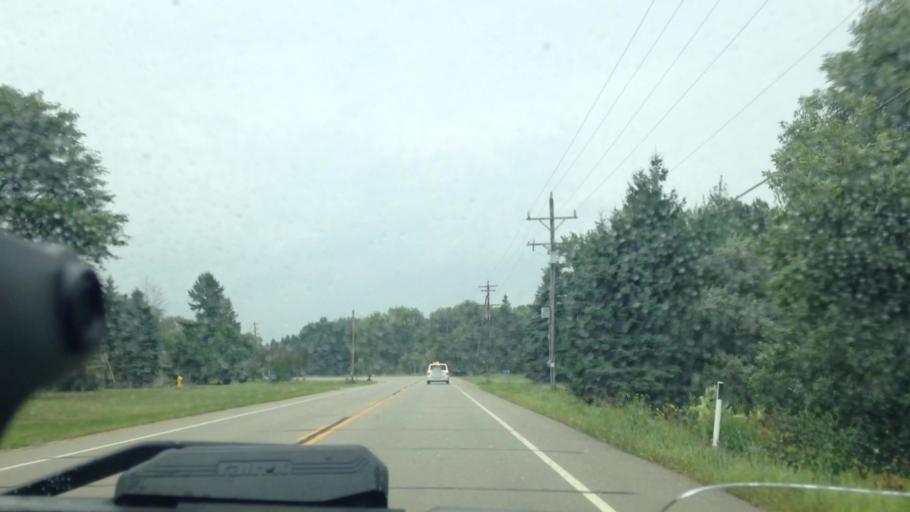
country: US
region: Wisconsin
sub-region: Washington County
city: Slinger
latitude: 43.3436
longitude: -88.3044
